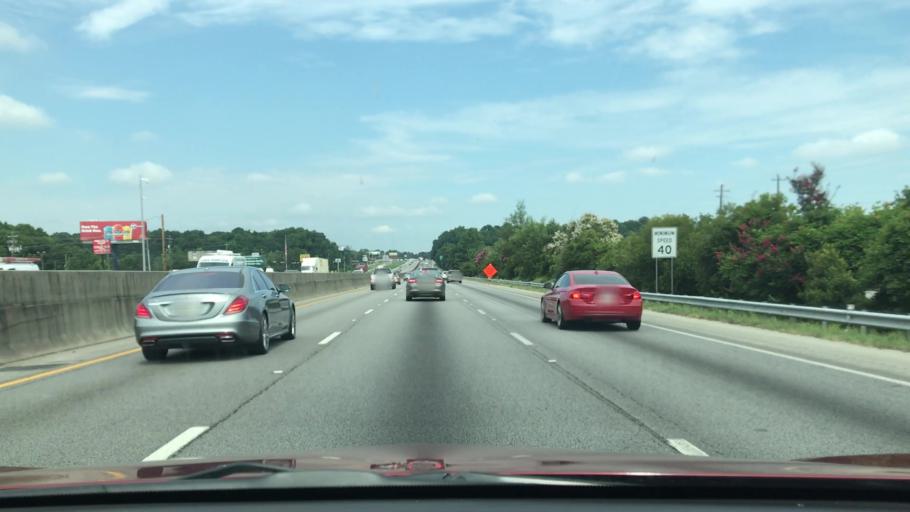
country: US
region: Georgia
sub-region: Rockdale County
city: Conyers
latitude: 33.6699
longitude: -84.0429
